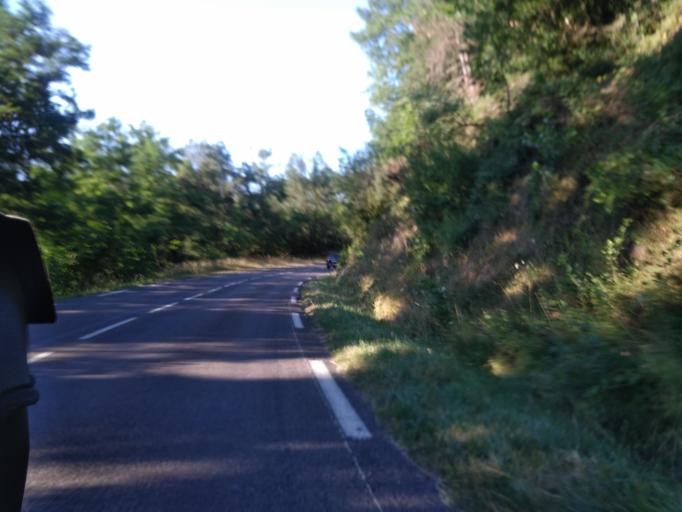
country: FR
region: Rhone-Alpes
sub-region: Departement de la Loire
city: Rozier-en-Donzy
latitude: 45.7457
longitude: 4.3015
